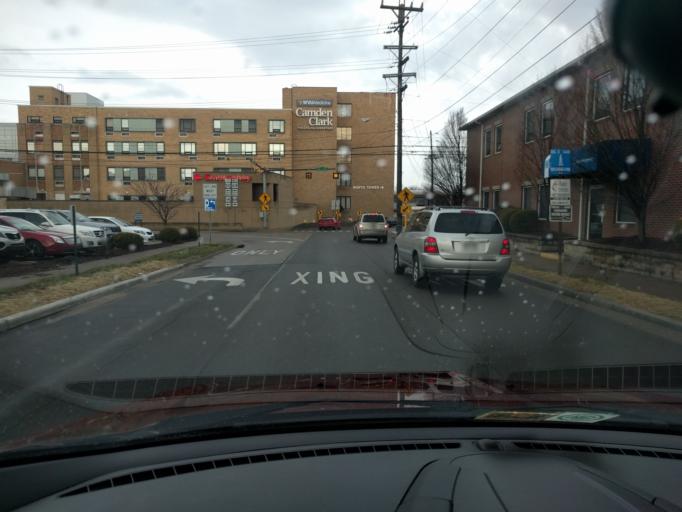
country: US
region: West Virginia
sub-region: Wood County
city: Parkersburg
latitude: 39.2690
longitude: -81.5587
